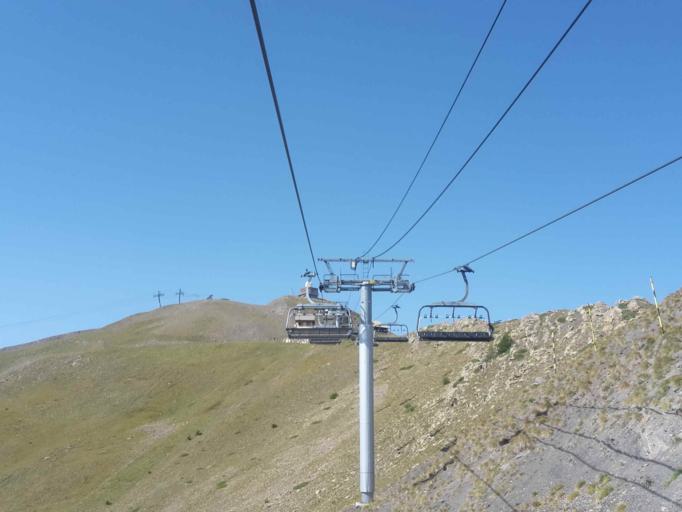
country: FR
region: Provence-Alpes-Cote d'Azur
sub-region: Departement des Hautes-Alpes
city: Guillestre
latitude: 44.5884
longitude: 6.6581
